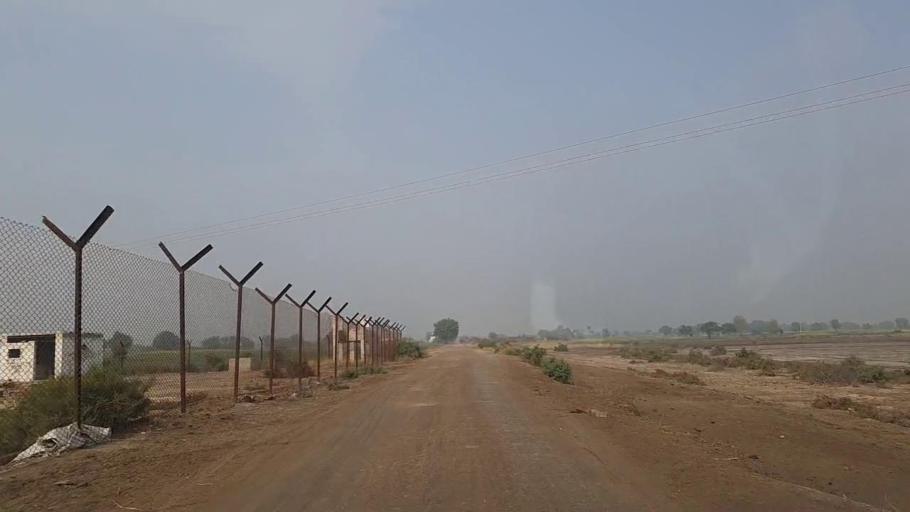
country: PK
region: Sindh
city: Sanghar
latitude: 26.1032
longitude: 68.8963
